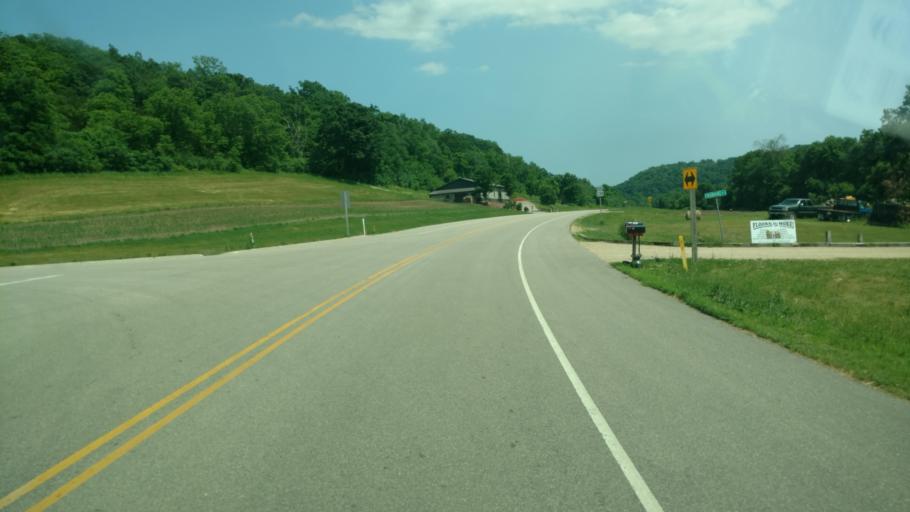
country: US
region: Wisconsin
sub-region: Vernon County
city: Viroqua
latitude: 43.4690
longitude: -90.7327
